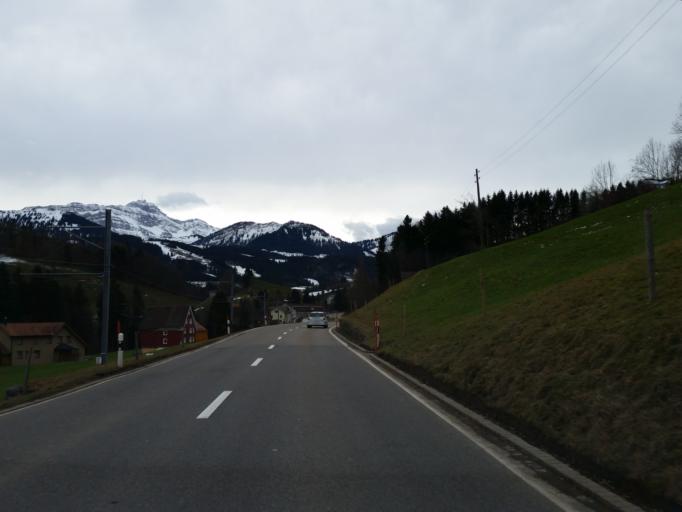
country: CH
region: Appenzell Ausserrhoden
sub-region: Bezirk Hinterland
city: Waldstatt
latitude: 47.3398
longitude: 9.2914
